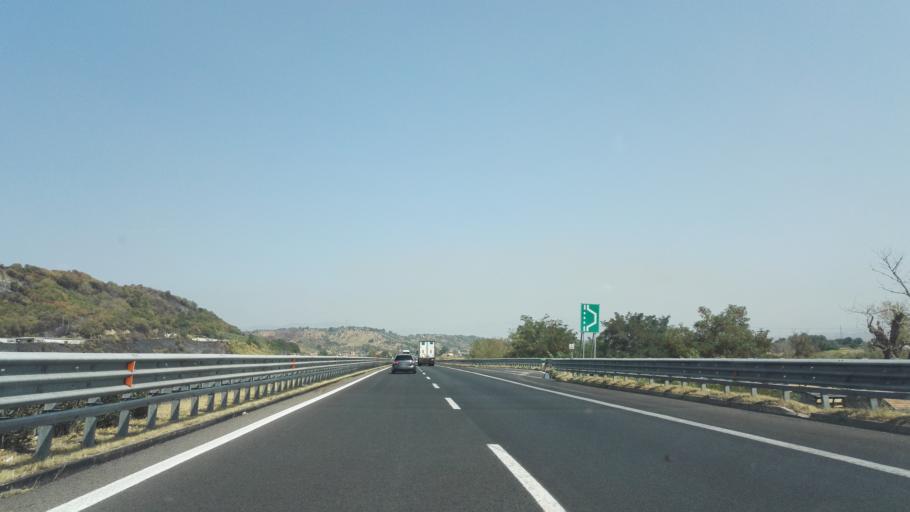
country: IT
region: Calabria
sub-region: Provincia di Cosenza
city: Sartano
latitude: 39.4820
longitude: 16.2149
